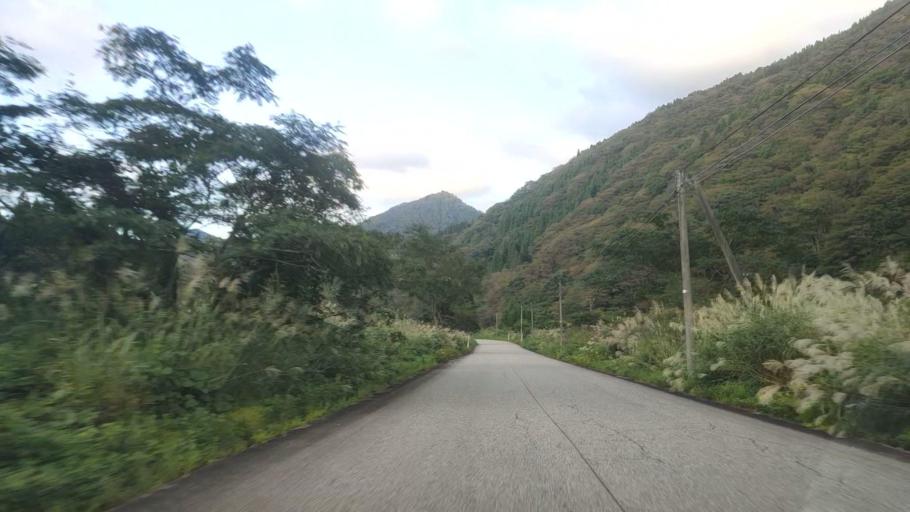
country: JP
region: Toyama
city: Yatsuomachi-higashikumisaka
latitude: 36.4644
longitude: 137.0852
